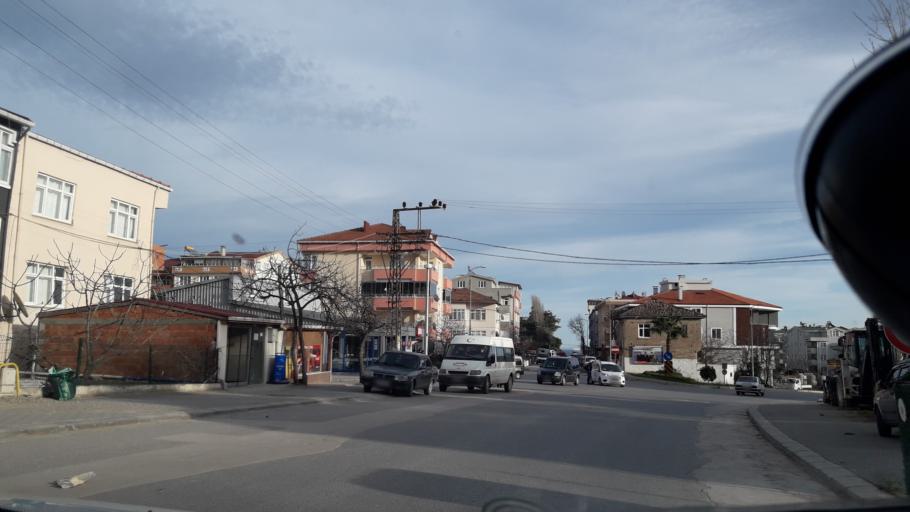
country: TR
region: Sinop
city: Gerze
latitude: 41.8062
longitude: 35.1895
